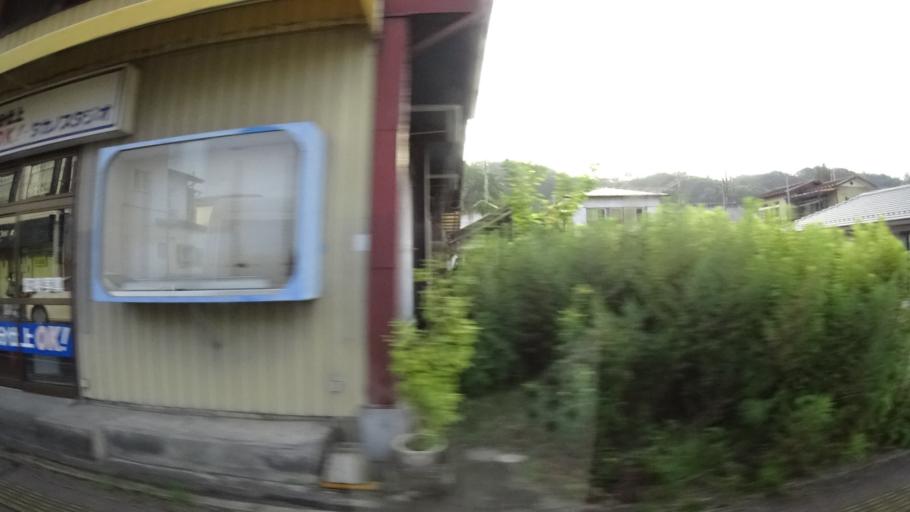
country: JP
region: Tochigi
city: Karasuyama
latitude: 36.6491
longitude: 140.1521
